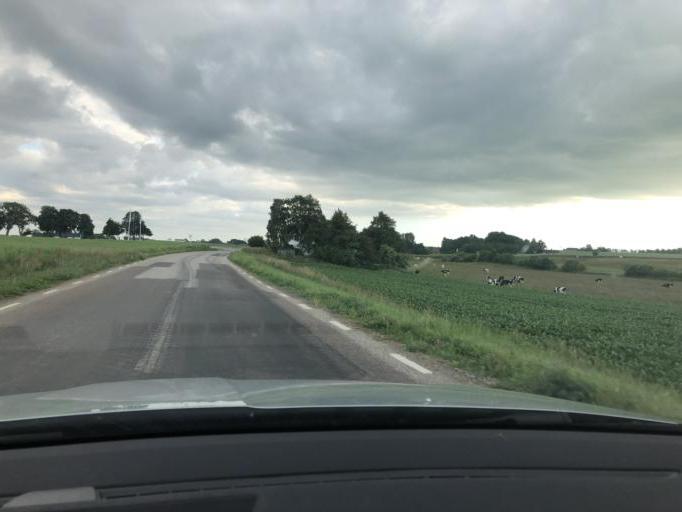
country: SE
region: Skane
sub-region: Simrishamns Kommun
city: Simrishamn
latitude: 55.5037
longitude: 14.2239
